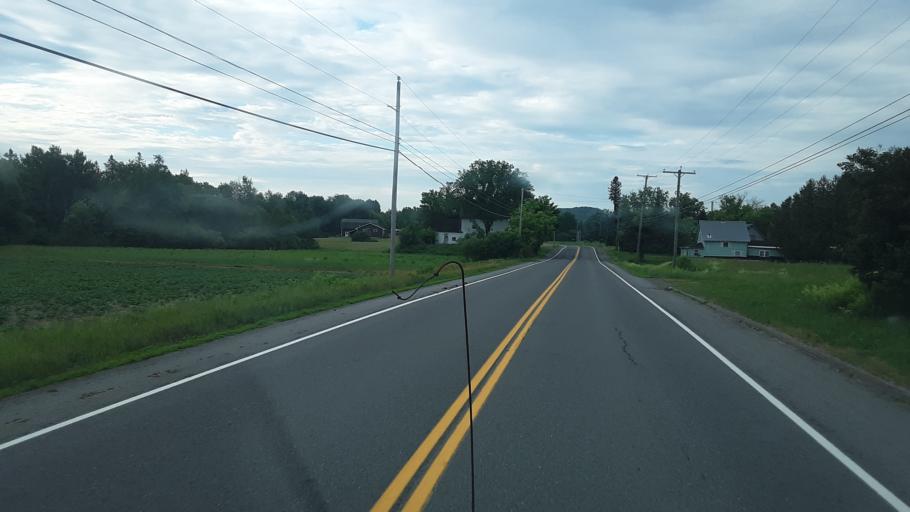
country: US
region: Maine
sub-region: Penobscot County
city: Patten
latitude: 45.9065
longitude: -68.4354
